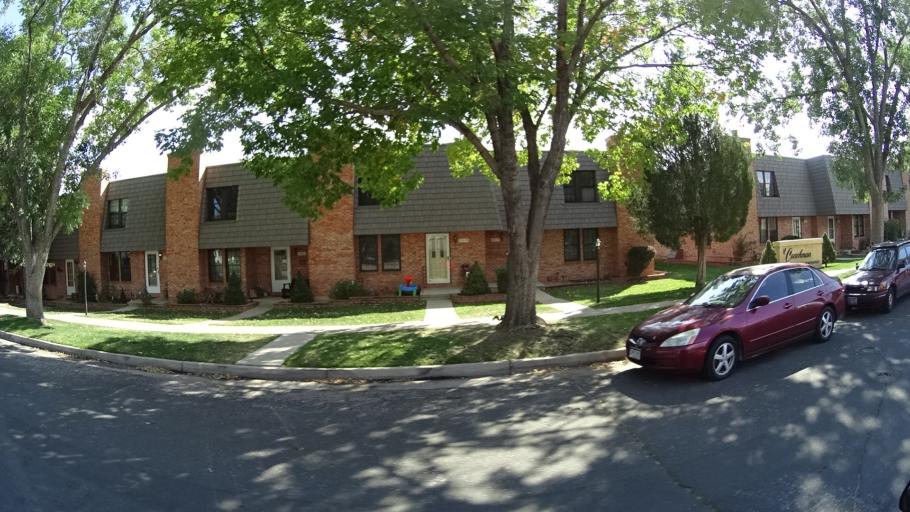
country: US
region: Colorado
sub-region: El Paso County
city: Cimarron Hills
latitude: 38.8625
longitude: -104.7596
